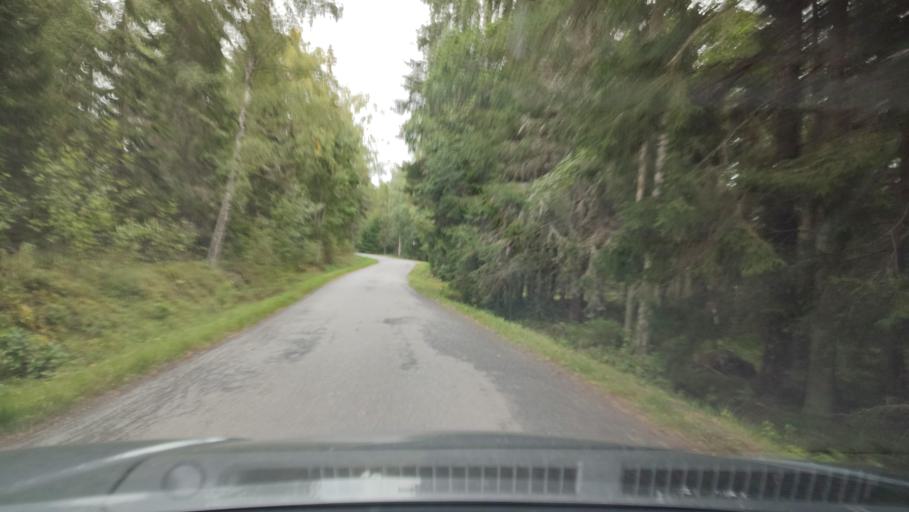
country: FI
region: Ostrobothnia
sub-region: Sydosterbotten
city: Kristinestad
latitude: 62.2523
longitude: 21.3537
